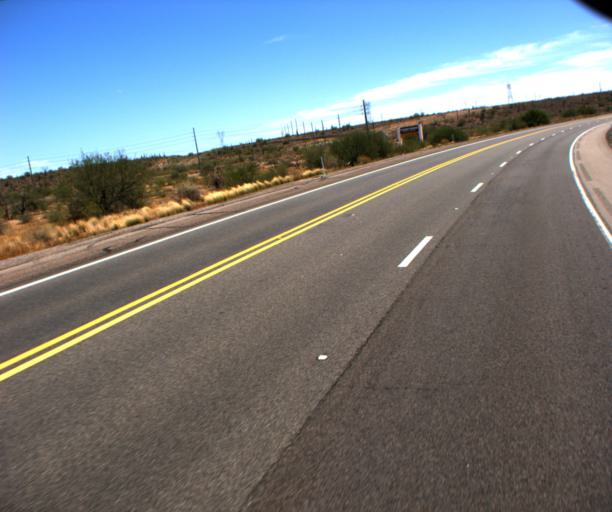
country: US
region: Arizona
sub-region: Maricopa County
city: Anthem
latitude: 33.8274
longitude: -112.2615
